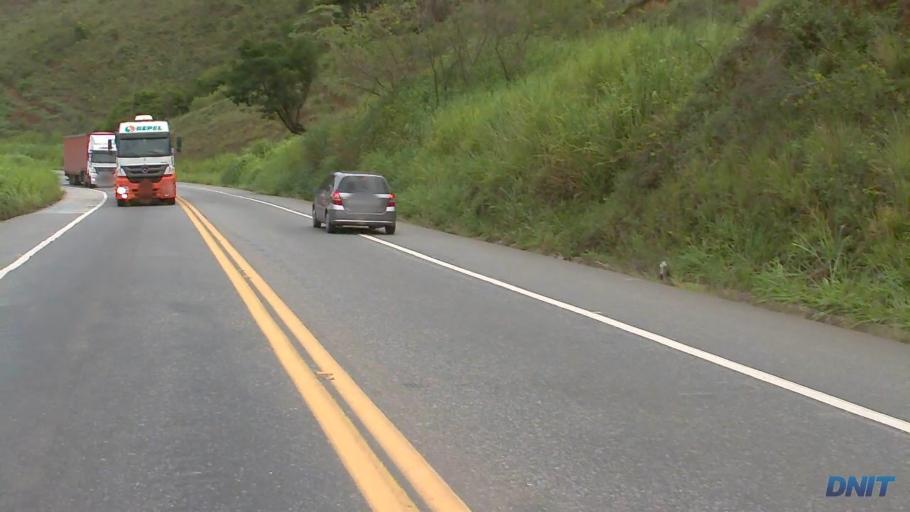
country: BR
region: Minas Gerais
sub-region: Nova Era
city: Nova Era
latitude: -19.6866
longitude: -42.9892
